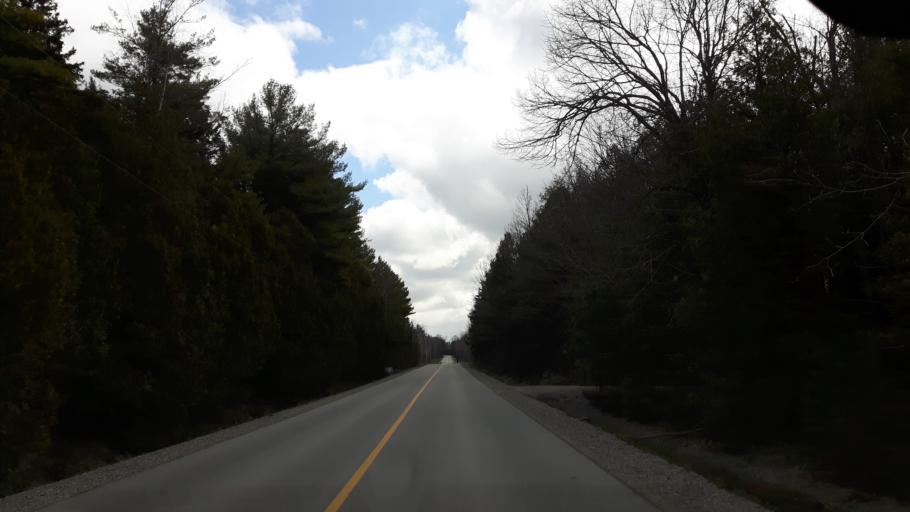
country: CA
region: Ontario
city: Bluewater
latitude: 43.5757
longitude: -81.7027
